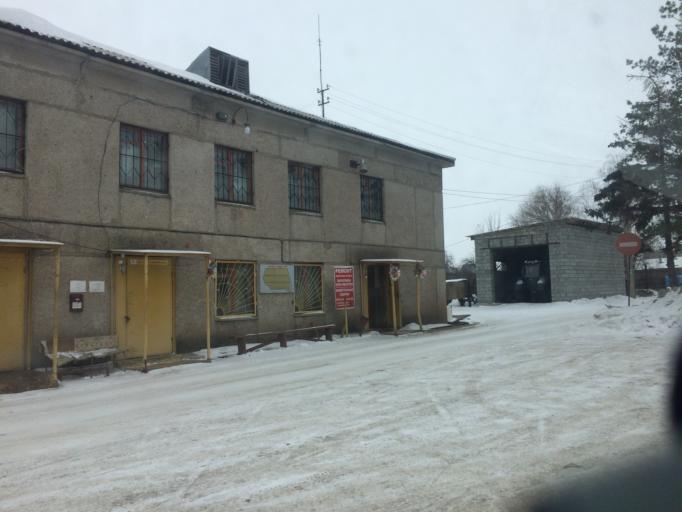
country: RU
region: Chelyabinsk
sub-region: Gorod Magnitogorsk
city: Magnitogorsk
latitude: 53.3571
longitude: 58.9993
